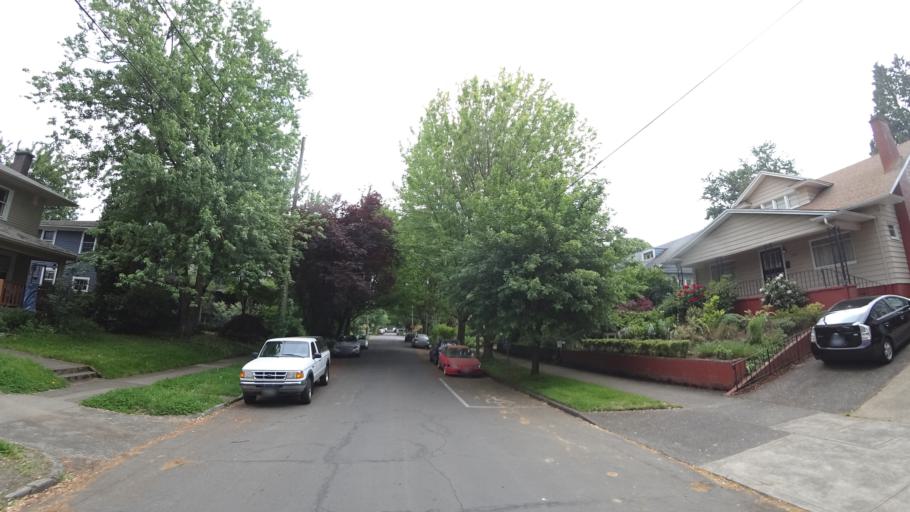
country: US
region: Oregon
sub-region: Multnomah County
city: Portland
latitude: 45.5461
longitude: -122.6514
